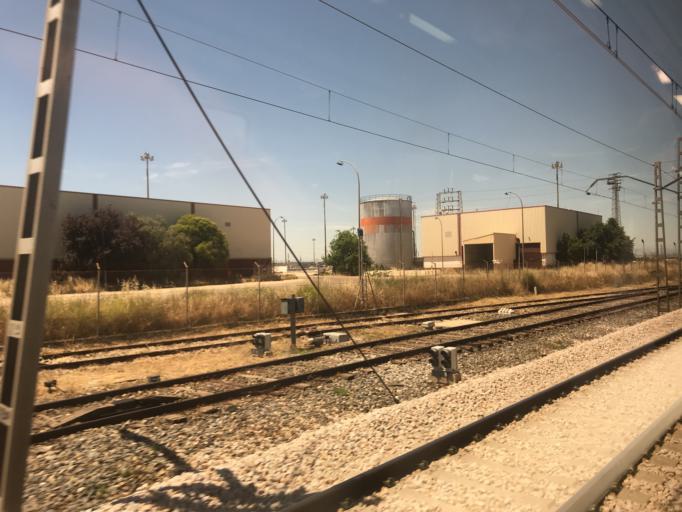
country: ES
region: Madrid
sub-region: Provincia de Madrid
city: Pinto
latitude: 40.2538
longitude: -3.7042
